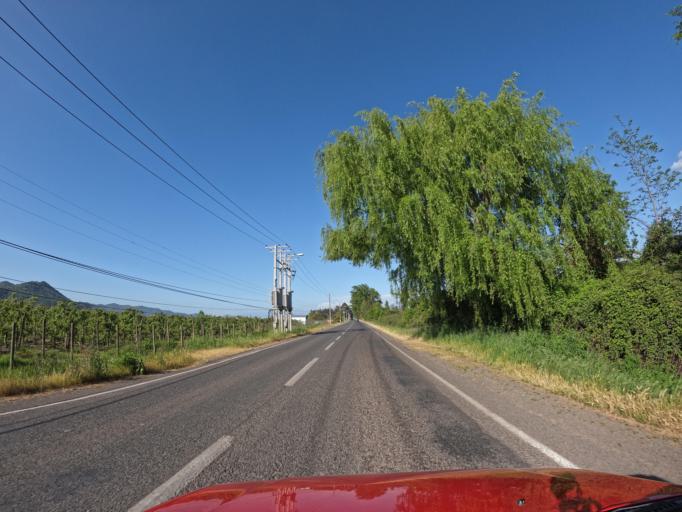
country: CL
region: Maule
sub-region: Provincia de Curico
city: Teno
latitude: -34.8687
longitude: -71.2146
